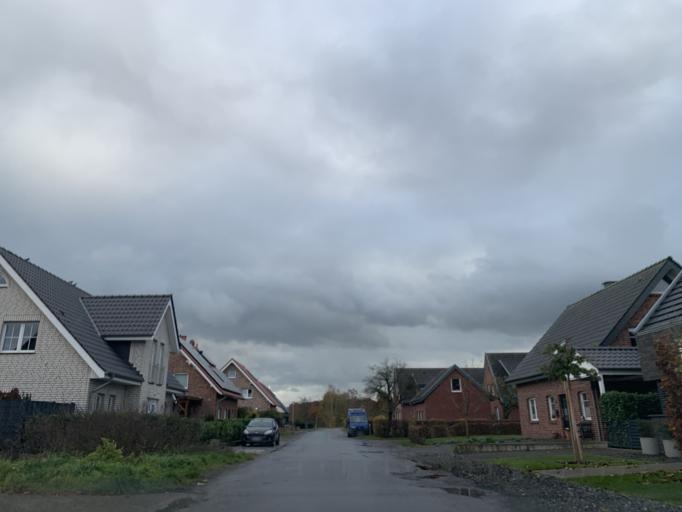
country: DE
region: North Rhine-Westphalia
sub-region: Regierungsbezirk Munster
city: Steinfurt
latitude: 52.1142
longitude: 7.3812
